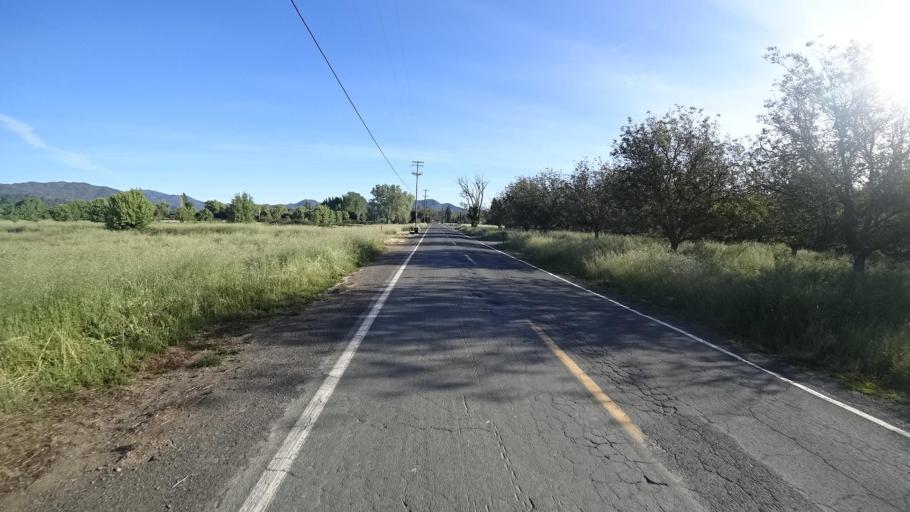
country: US
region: California
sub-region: Lake County
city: North Lakeport
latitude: 39.0777
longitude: -122.9498
